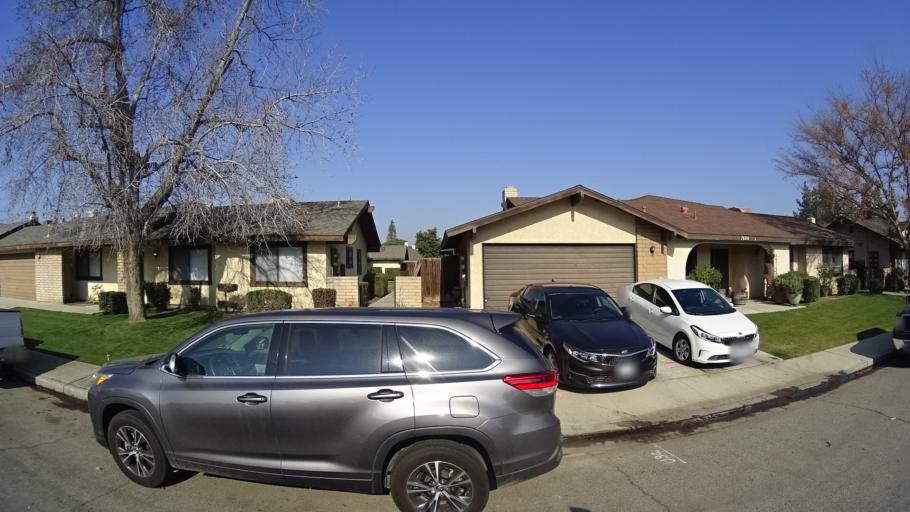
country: US
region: California
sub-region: Kern County
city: Greenacres
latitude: 35.3546
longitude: -119.0881
